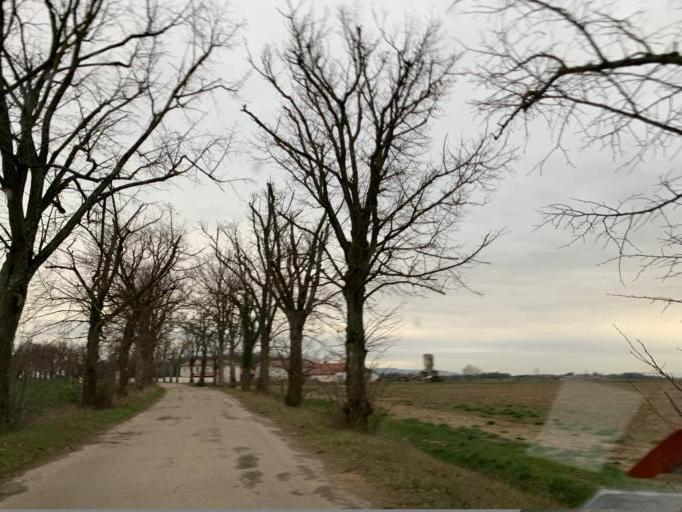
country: FR
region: Rhone-Alpes
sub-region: Departement de l'Ain
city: Tramoyes
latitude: 45.8744
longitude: 4.9978
